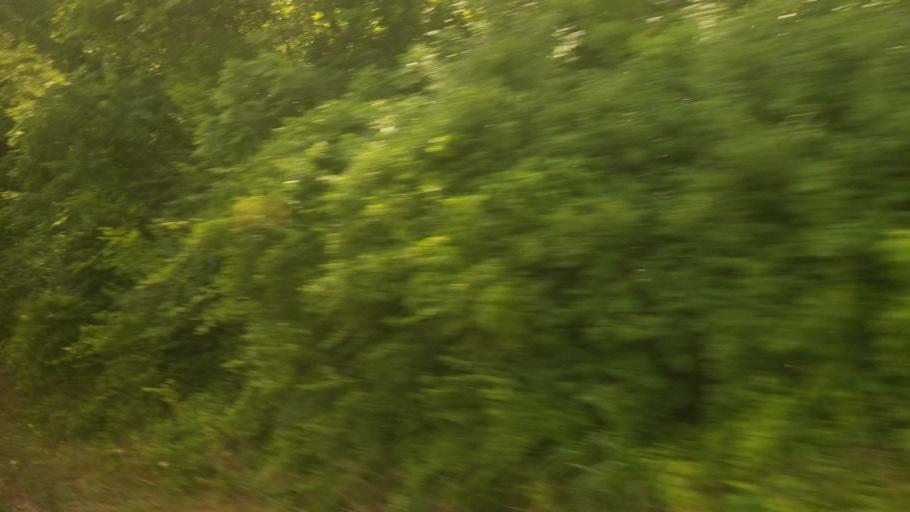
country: US
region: Missouri
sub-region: Jackson County
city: Sugar Creek
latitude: 39.1539
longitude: -94.4069
